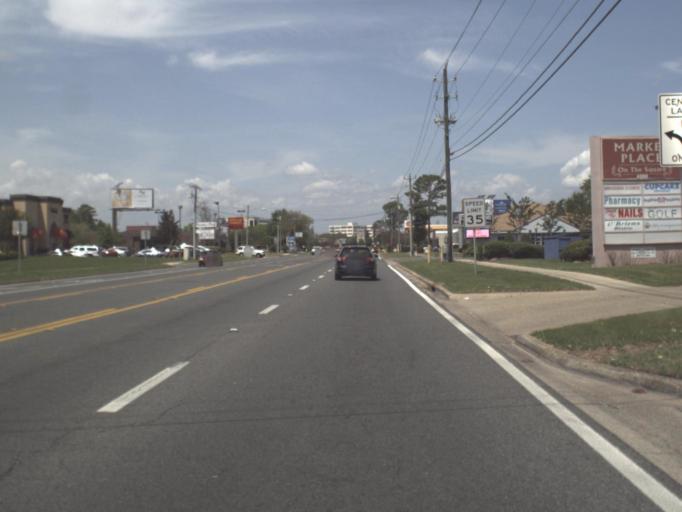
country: US
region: Florida
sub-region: Escambia County
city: Goulding
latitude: 30.4663
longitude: -87.2045
